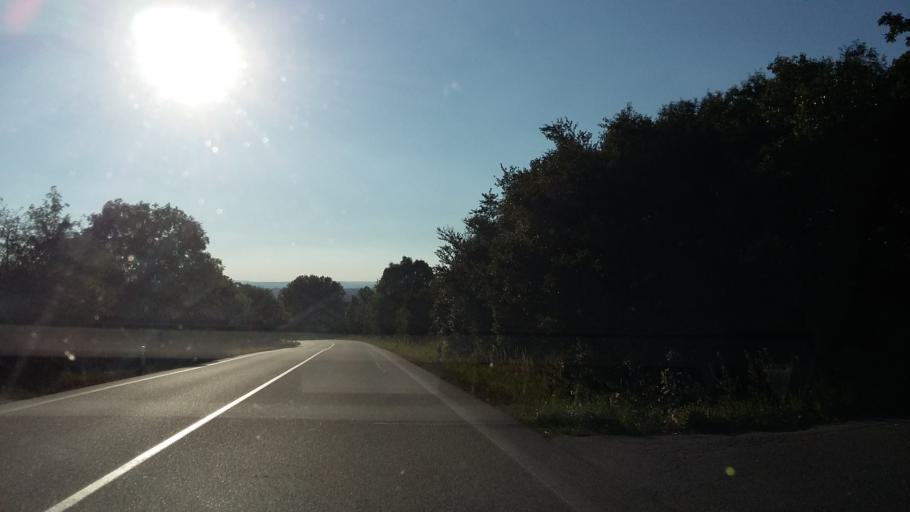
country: CZ
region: Vysocina
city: Luka nad Jihlavou
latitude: 49.3966
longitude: 15.7301
